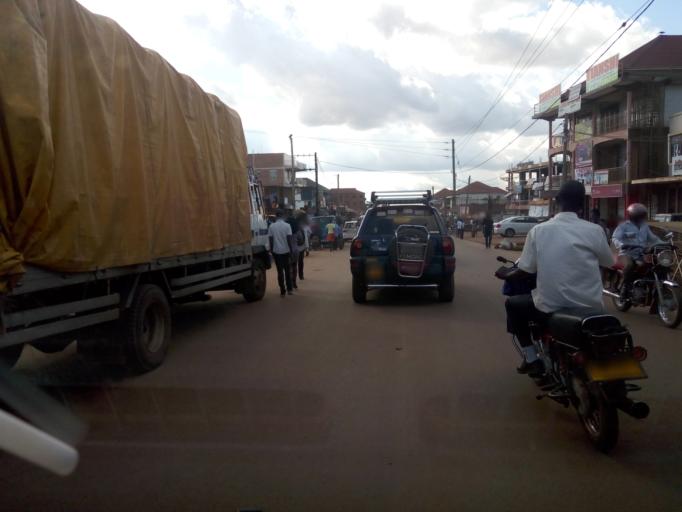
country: UG
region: Central Region
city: Kampala Central Division
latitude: 0.3850
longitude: 32.5546
